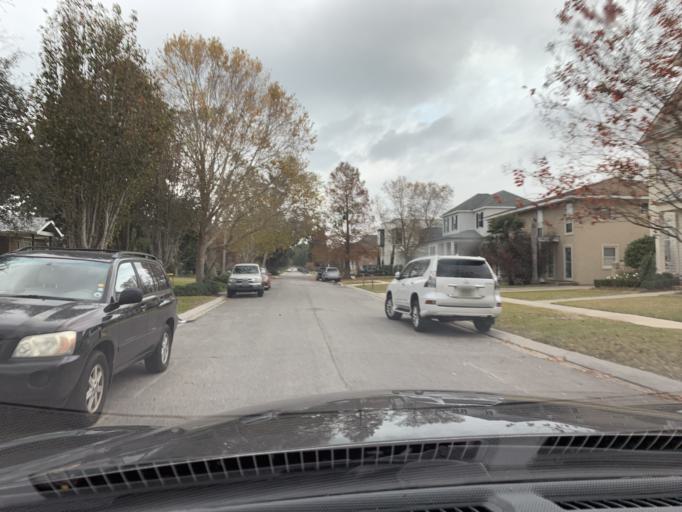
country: US
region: Louisiana
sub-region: Jefferson Parish
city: Metairie
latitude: 30.0124
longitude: -90.1006
